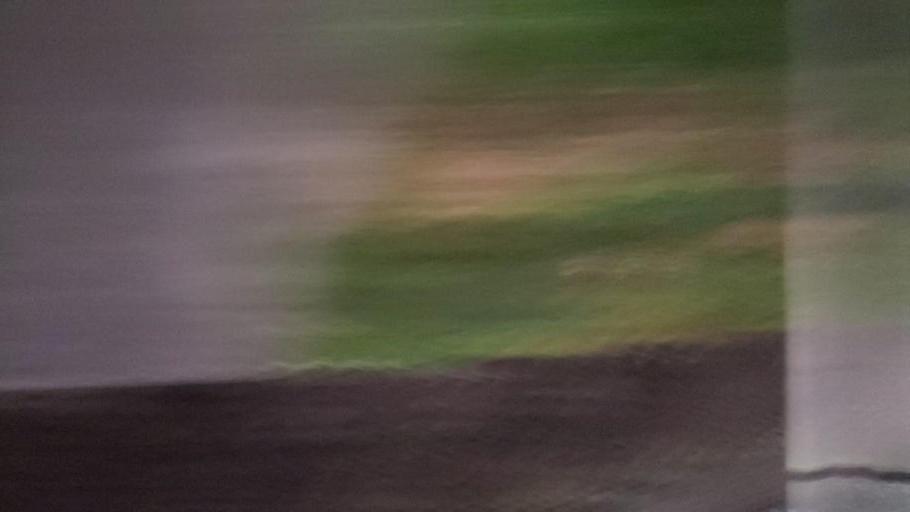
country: JP
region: Tokushima
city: Kamojimacho-jogejima
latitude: 34.0925
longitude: 134.2845
